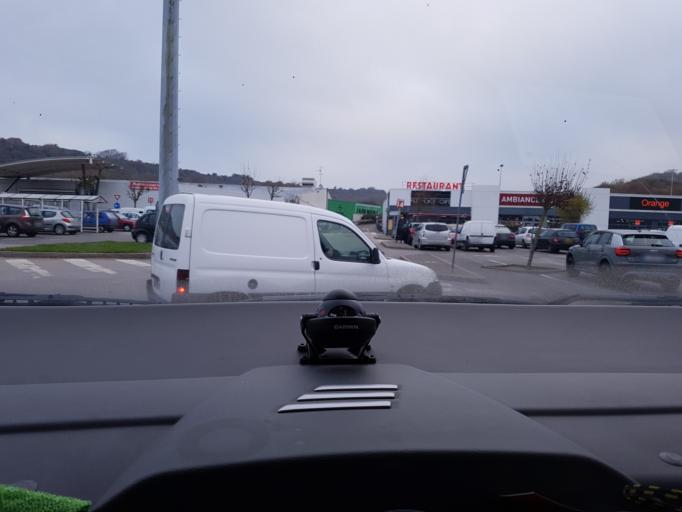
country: FR
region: Haute-Normandie
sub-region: Departement de la Seine-Maritime
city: Eu
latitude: 50.0612
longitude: 1.4087
